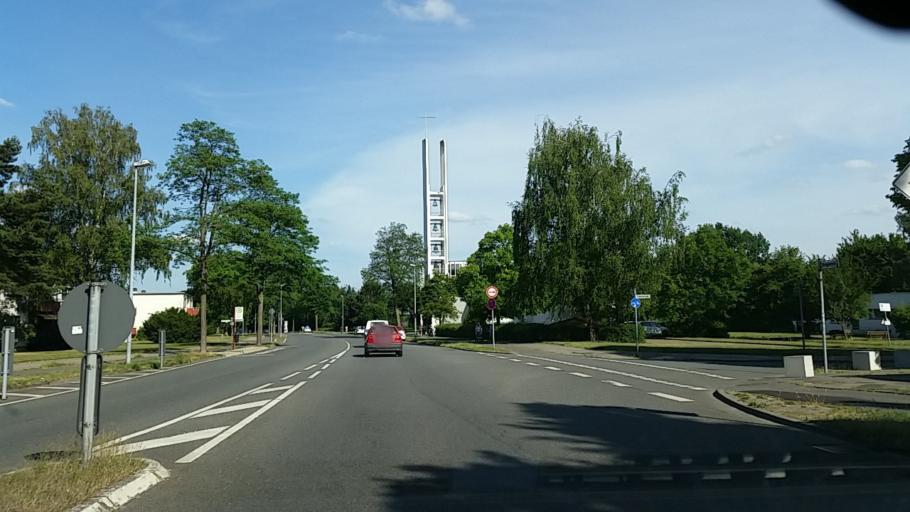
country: DE
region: Lower Saxony
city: Wolfsburg
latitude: 52.4102
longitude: 10.7678
